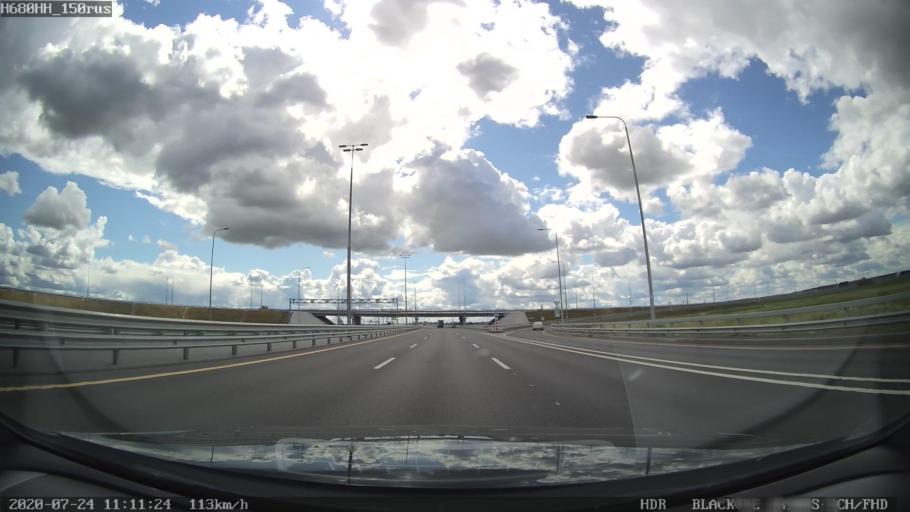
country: RU
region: Leningrad
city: Fedorovskoye
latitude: 59.7234
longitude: 30.5150
